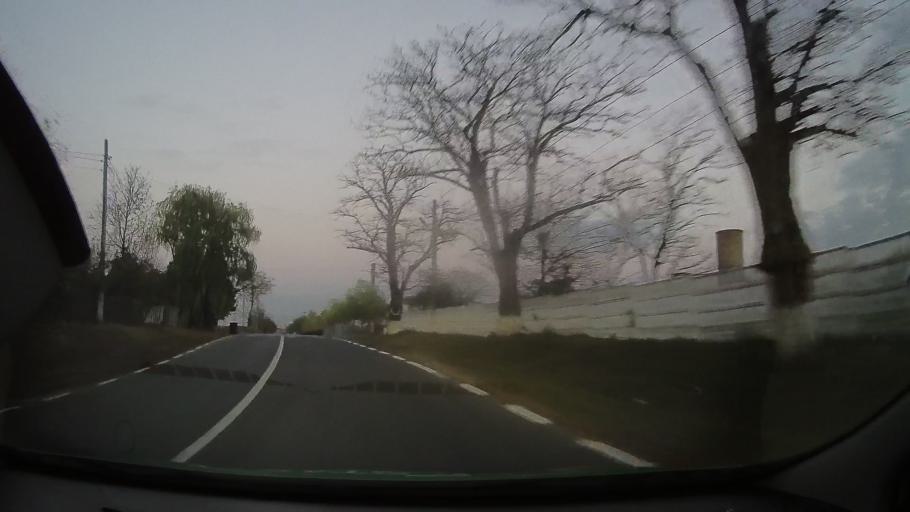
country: RO
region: Constanta
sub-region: Comuna Baneasa
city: Baneasa
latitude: 44.0673
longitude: 27.7131
